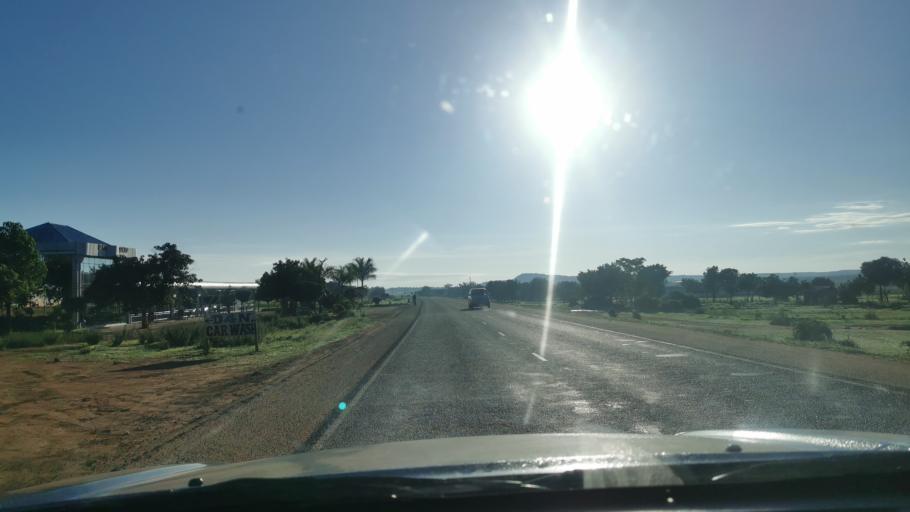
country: TZ
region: Shinyanga
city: Kahama
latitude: -3.8383
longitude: 32.6370
